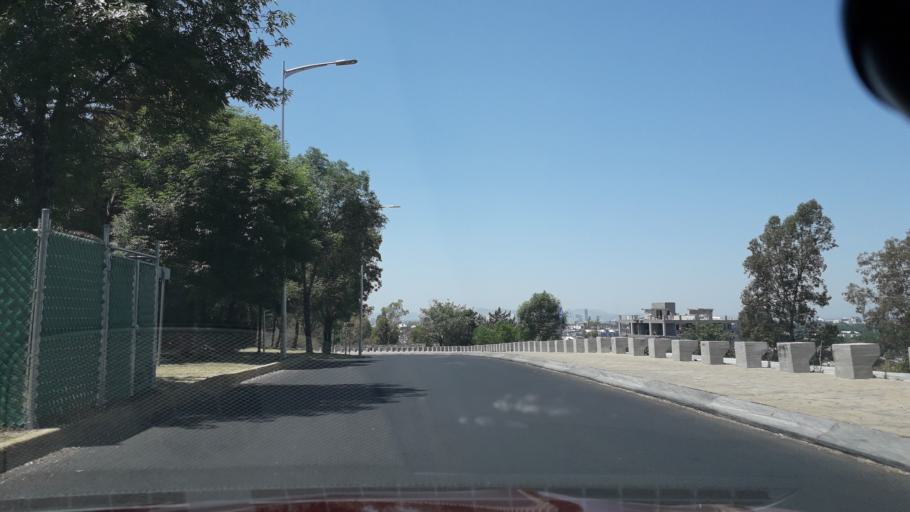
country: MX
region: Puebla
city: Puebla
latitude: 19.0585
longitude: -98.1876
